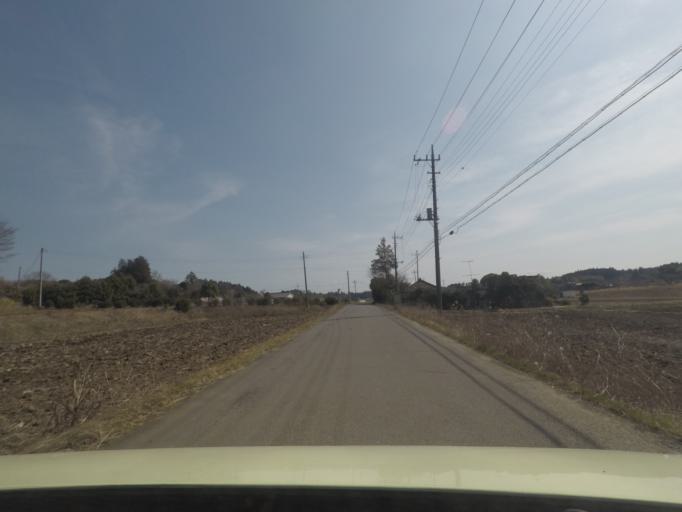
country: JP
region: Ibaraki
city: Ishioka
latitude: 36.1952
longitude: 140.3340
